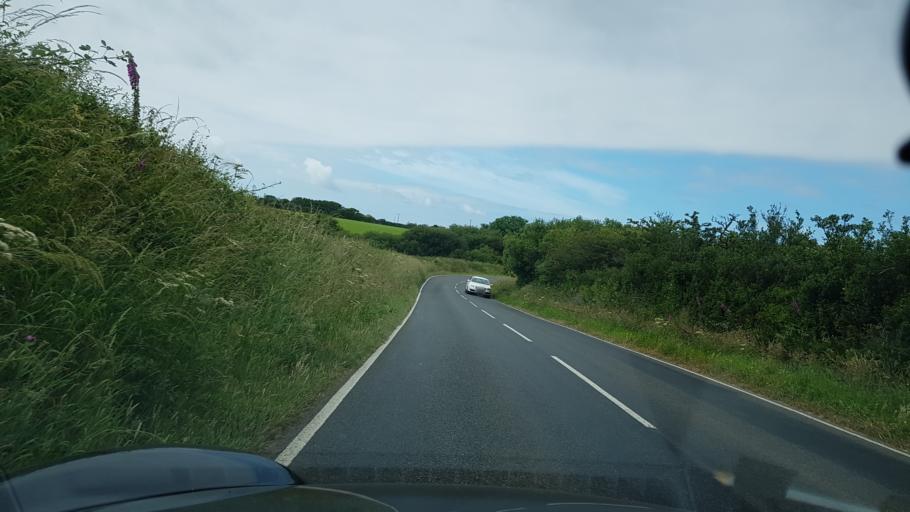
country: GB
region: Wales
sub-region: Pembrokeshire
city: Johnston
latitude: 51.7791
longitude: -5.0377
